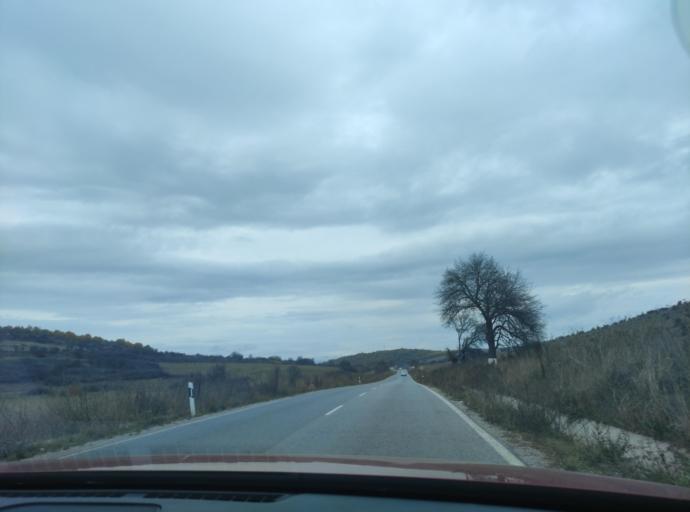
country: BG
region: Sofiya
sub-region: Obshtina Godech
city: Godech
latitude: 42.9566
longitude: 23.1562
